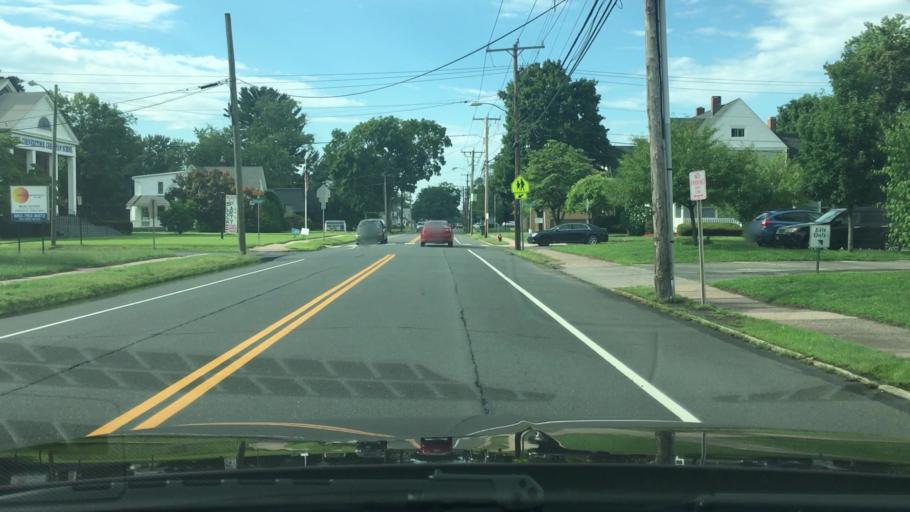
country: US
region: Connecticut
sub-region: Hartford County
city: Manchester
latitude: 41.7852
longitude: -72.5236
